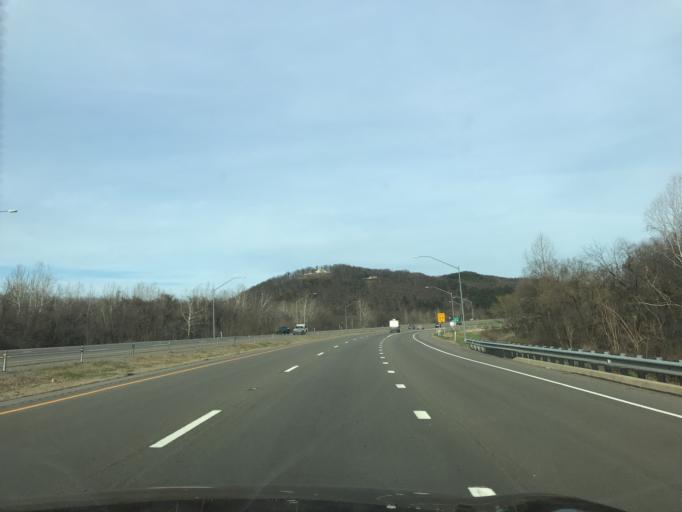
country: US
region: Pennsylvania
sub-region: Lycoming County
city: Montoursville
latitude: 41.2641
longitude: -76.9230
